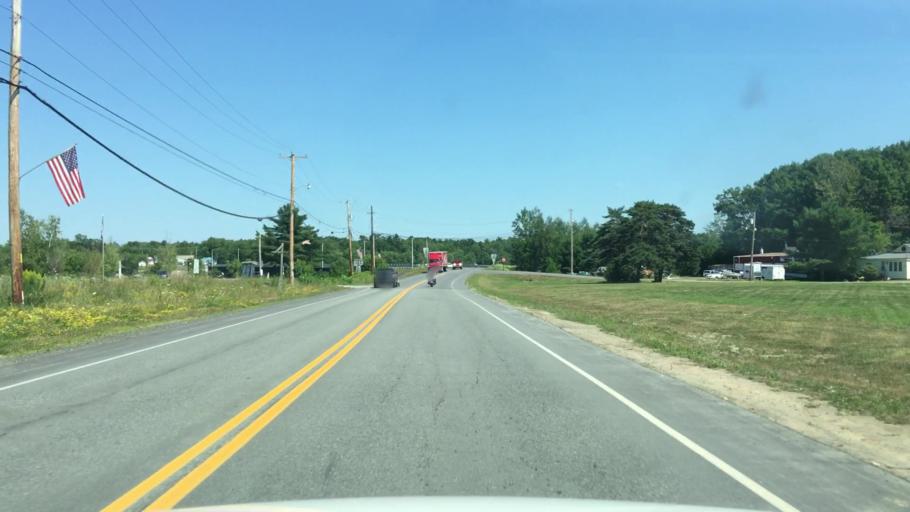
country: US
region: Maine
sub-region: Penobscot County
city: Howland
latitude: 45.2364
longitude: -68.6567
